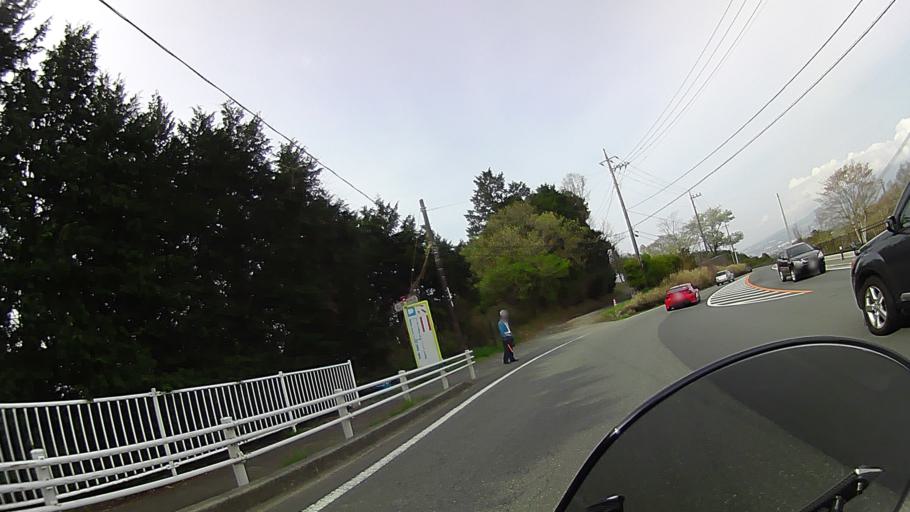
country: JP
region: Kanagawa
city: Hakone
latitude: 35.1489
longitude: 138.9828
